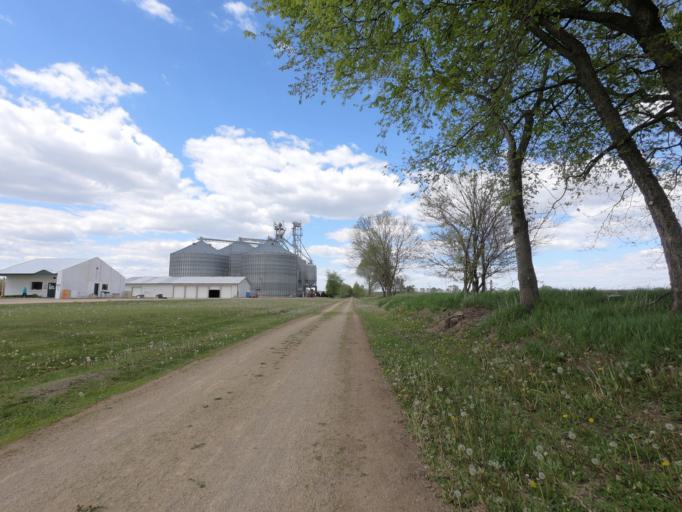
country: US
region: Wisconsin
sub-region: Dane County
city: Belleville
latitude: 42.8672
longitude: -89.5300
